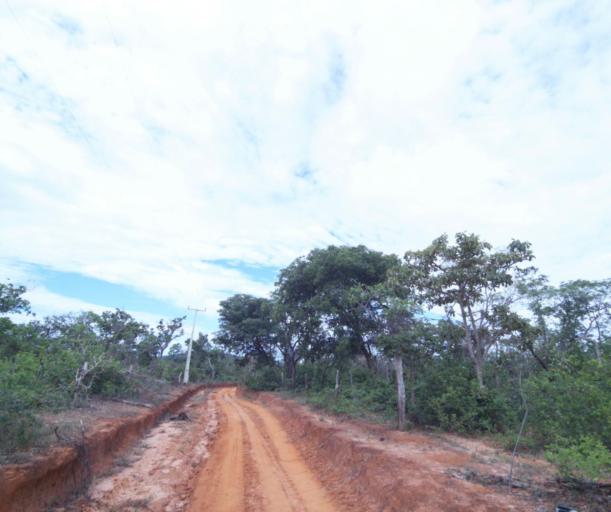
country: BR
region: Bahia
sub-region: Carinhanha
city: Carinhanha
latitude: -14.2368
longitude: -44.3793
